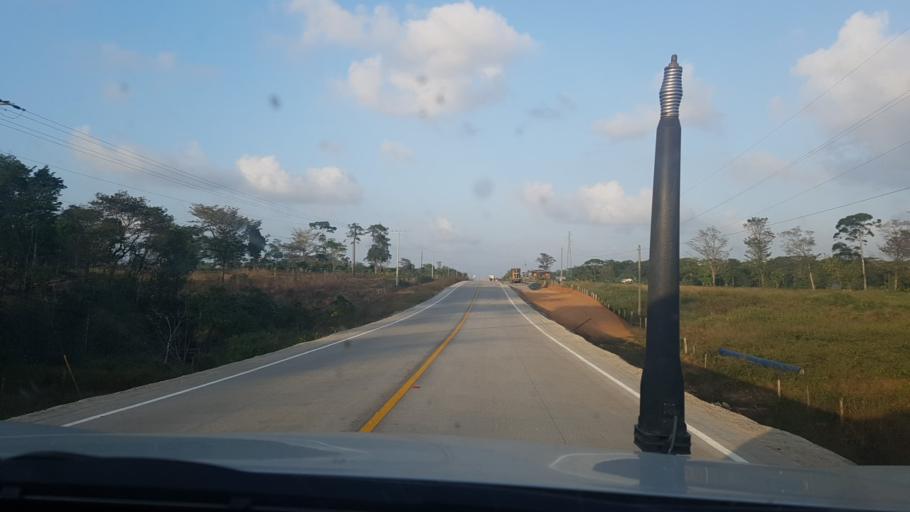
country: NI
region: Atlantico Sur
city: Bluefields
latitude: 11.9567
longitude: -83.9863
